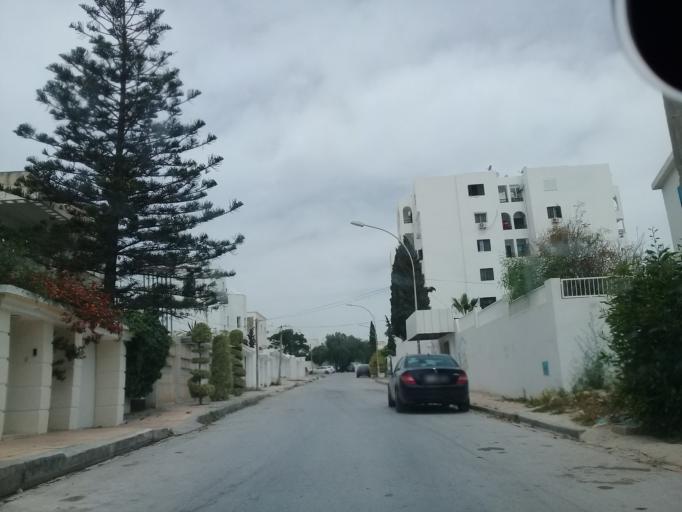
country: TN
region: Tunis
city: Tunis
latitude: 36.8354
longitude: 10.1570
